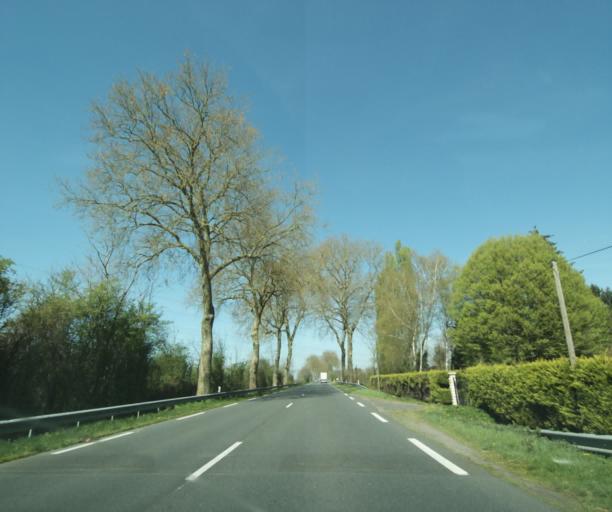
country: FR
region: Bourgogne
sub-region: Departement de la Nievre
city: Chantenay-Saint-Imbert
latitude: 46.6909
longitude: 3.2157
